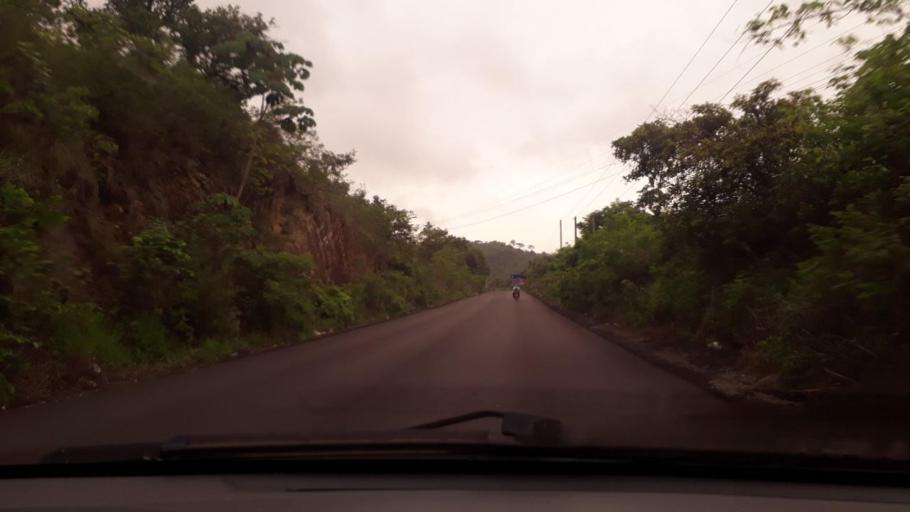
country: GT
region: Chiquimula
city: Concepcion Las Minas
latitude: 14.5579
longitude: -89.4635
